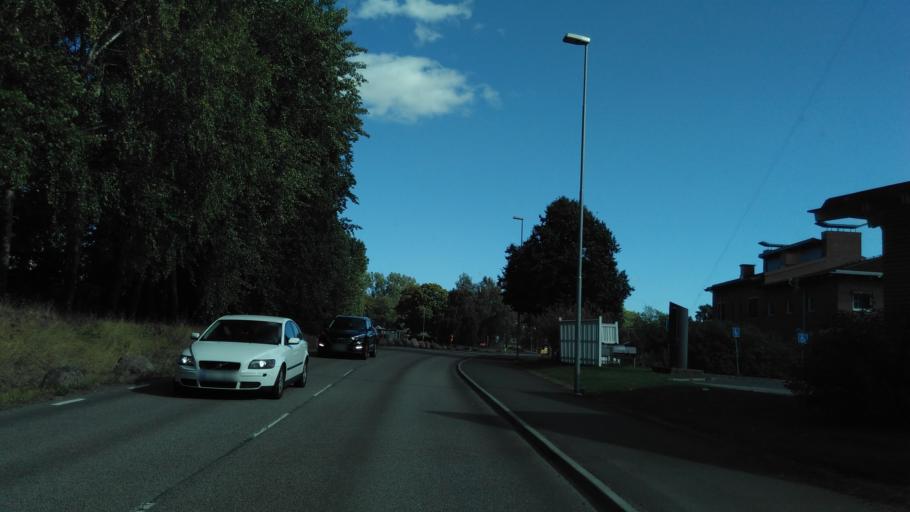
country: SE
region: Vaestra Goetaland
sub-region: Skovde Kommun
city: Skoevde
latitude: 58.4006
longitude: 13.8383
